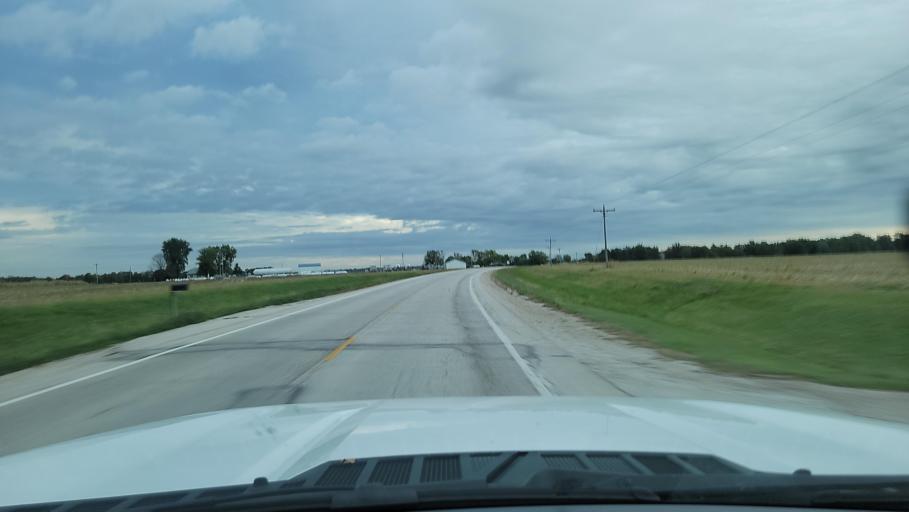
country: US
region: Illinois
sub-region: Schuyler County
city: Rushville
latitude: 40.0779
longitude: -90.6146
